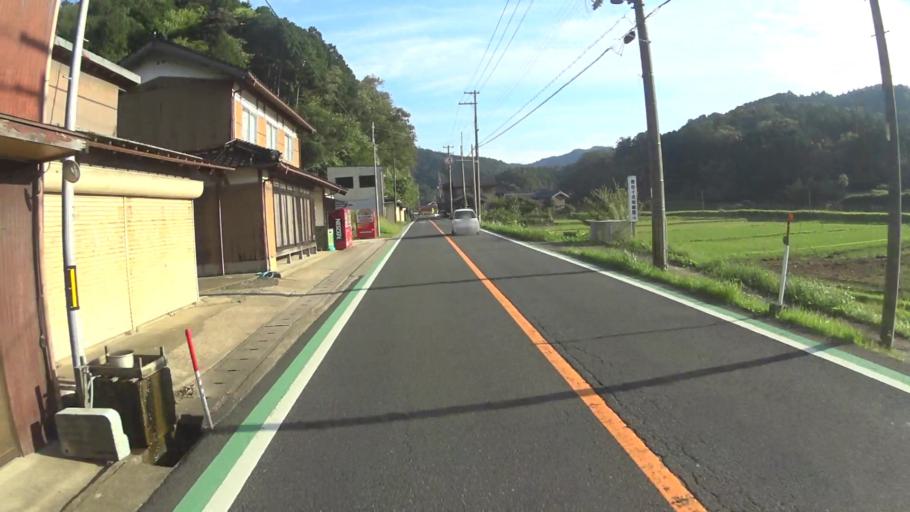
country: JP
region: Hyogo
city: Toyooka
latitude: 35.5967
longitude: 134.9054
